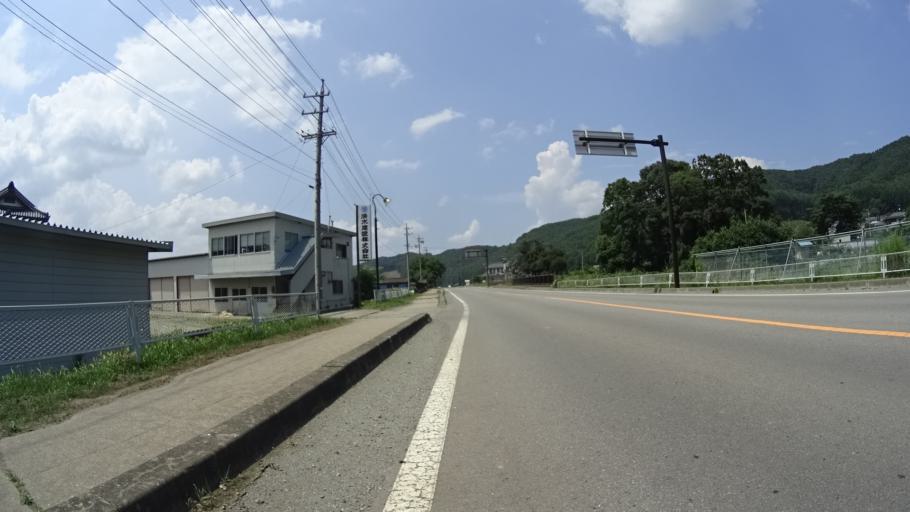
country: JP
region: Nagano
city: Saku
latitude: 36.1510
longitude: 138.5078
